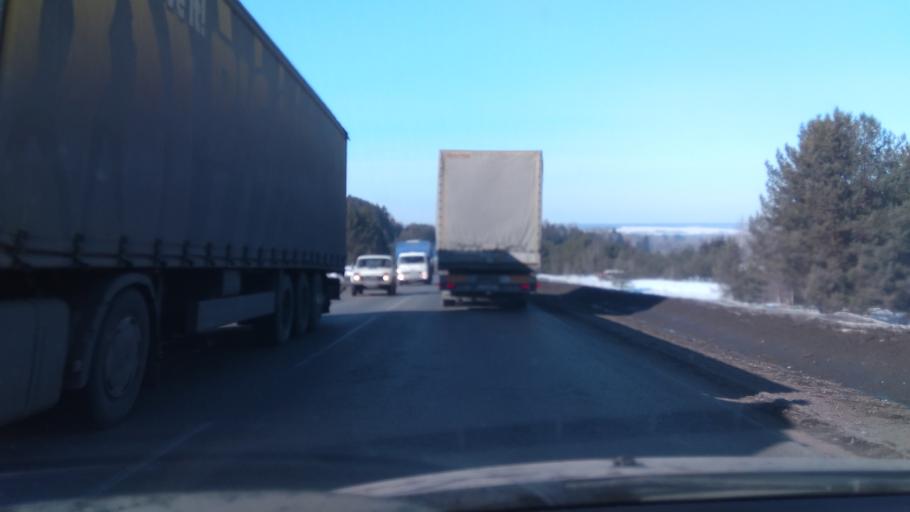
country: RU
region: Perm
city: Kungur
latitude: 57.4794
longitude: 56.7111
